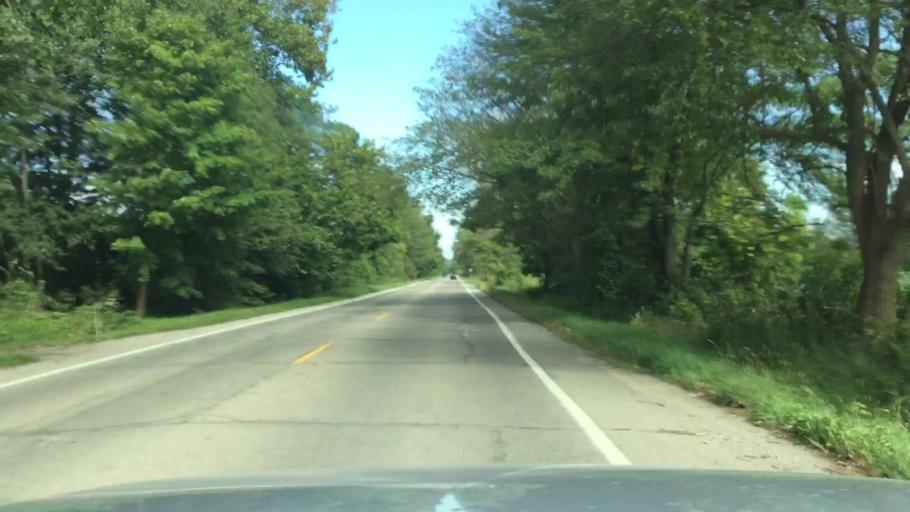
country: US
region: Michigan
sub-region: Wayne County
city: Belleville
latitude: 42.1829
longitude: -83.4832
